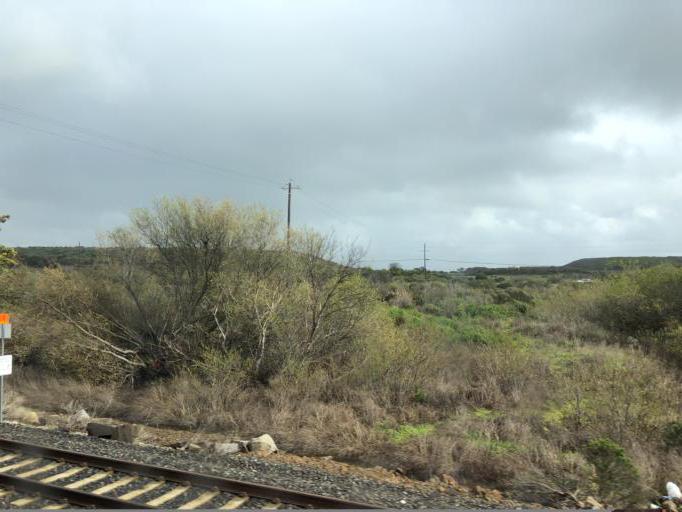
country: US
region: California
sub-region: San Mateo County
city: Brisbane
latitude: 37.6945
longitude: -122.4018
